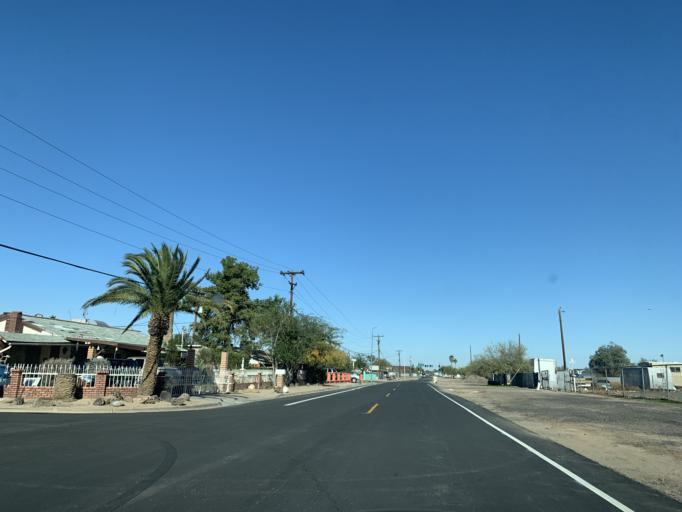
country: US
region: Arizona
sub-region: Maricopa County
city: Laveen
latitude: 33.3892
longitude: -112.1423
